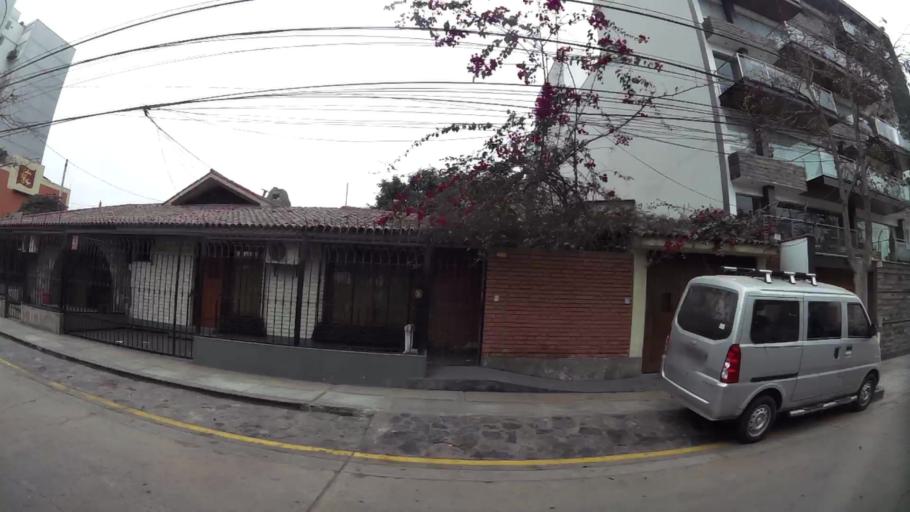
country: PE
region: Lima
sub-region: Lima
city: Surco
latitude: -12.1138
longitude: -76.9932
